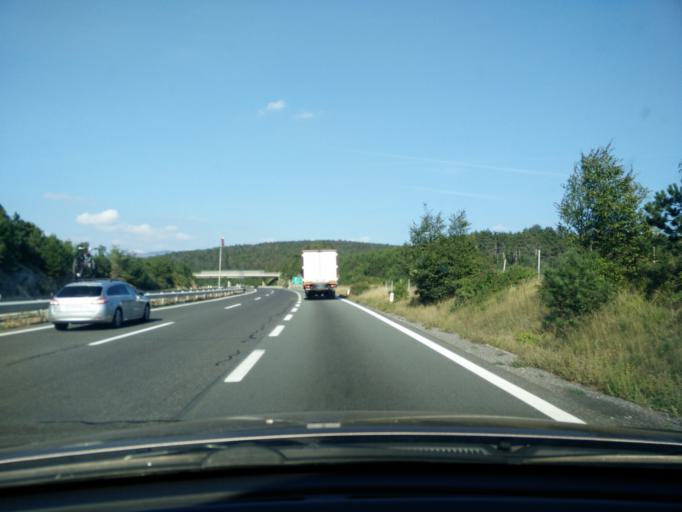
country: SI
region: Divaca
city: Divaca
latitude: 45.7038
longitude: 13.9985
